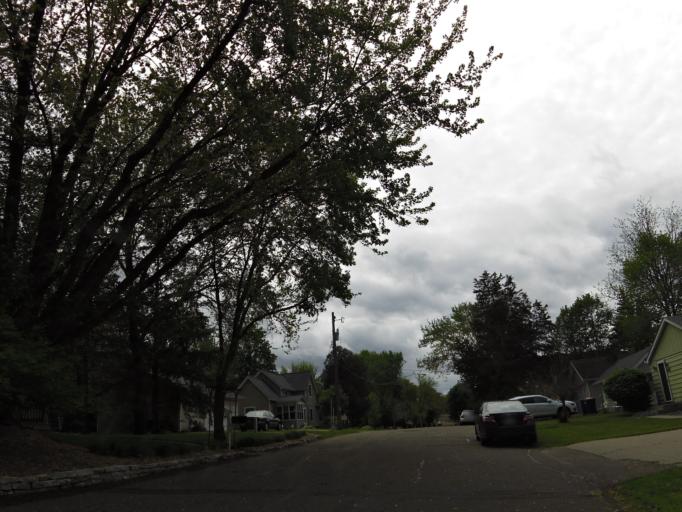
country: US
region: Wisconsin
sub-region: Saint Croix County
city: Hudson
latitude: 44.9830
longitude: -92.7452
